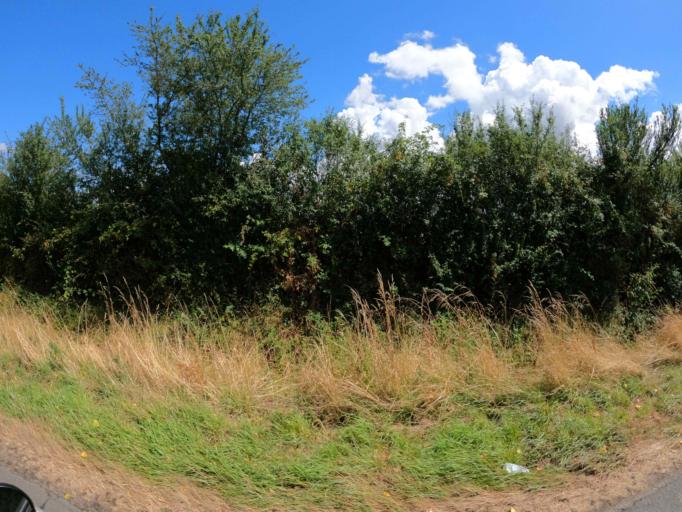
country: FR
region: Pays de la Loire
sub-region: Departement de la Sarthe
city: Brulon
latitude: 47.9250
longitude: -0.2633
